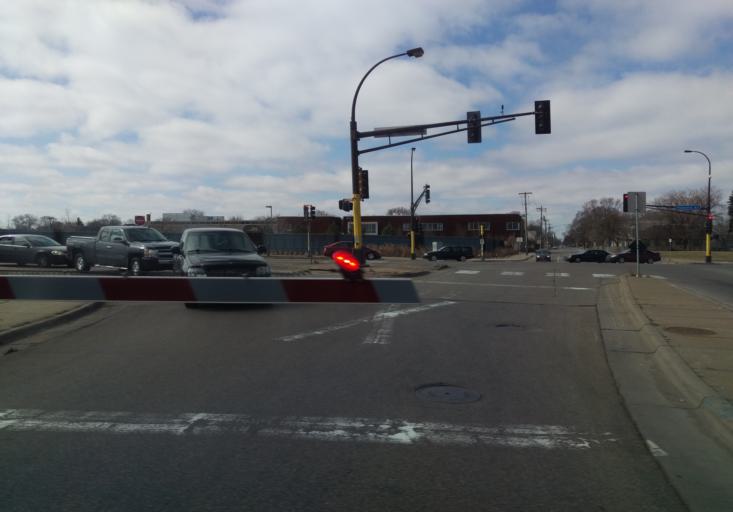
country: US
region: Minnesota
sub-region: Hennepin County
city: Minneapolis
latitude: 44.9556
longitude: -93.2425
